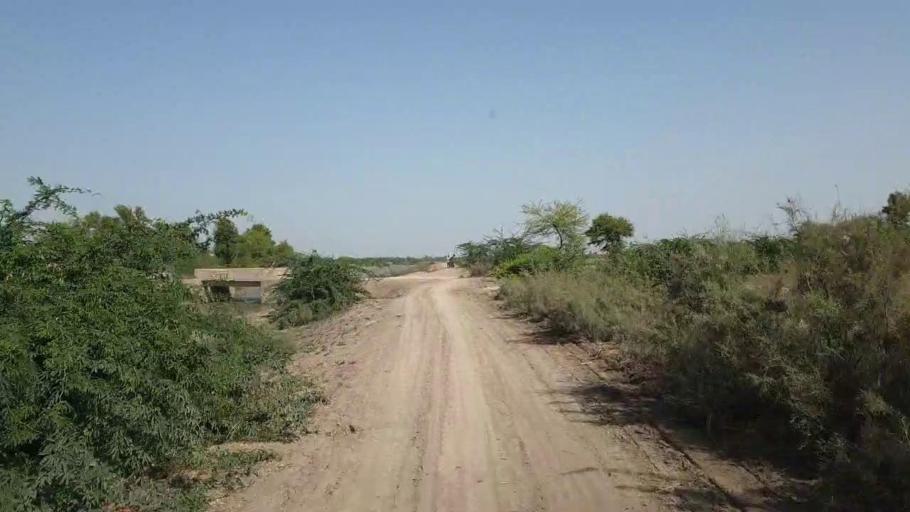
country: PK
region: Sindh
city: Tando Bago
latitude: 24.6683
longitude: 69.0681
